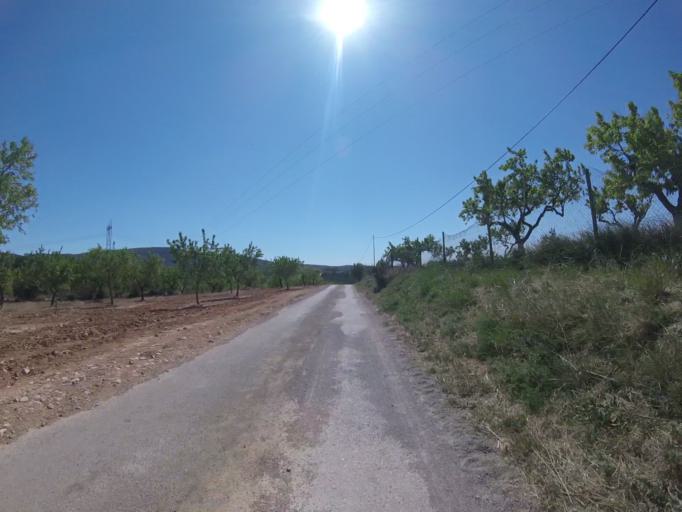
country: ES
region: Valencia
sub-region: Provincia de Castello
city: Cuevas de Vinroma
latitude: 40.3762
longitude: 0.1338
